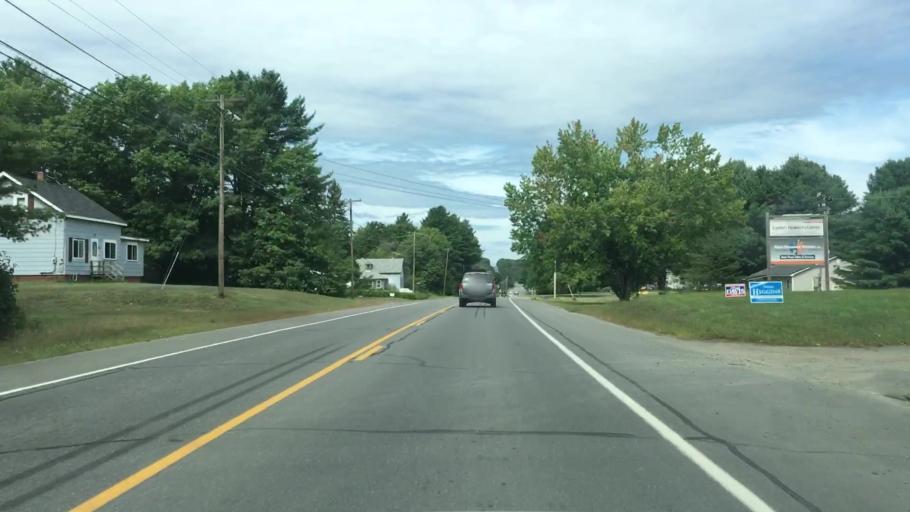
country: US
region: Maine
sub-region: Piscataquis County
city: Milo
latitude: 45.2663
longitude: -68.9941
